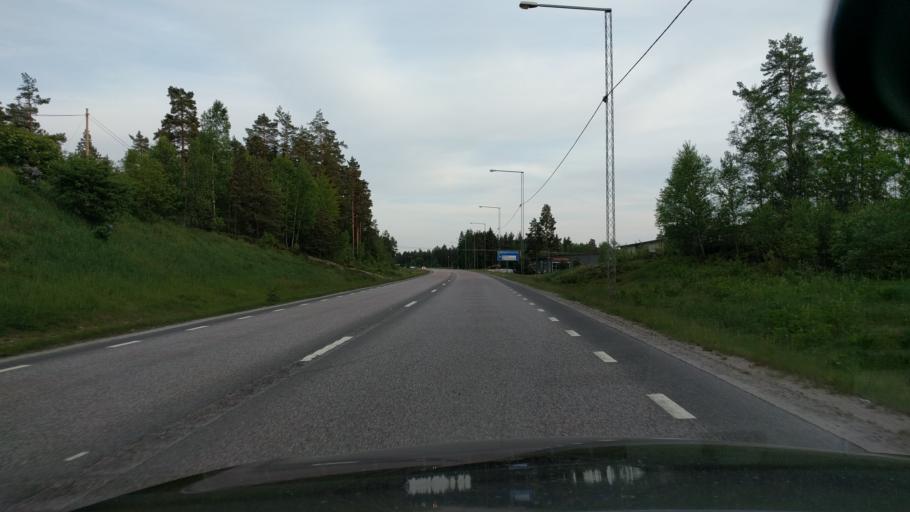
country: SE
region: Stockholm
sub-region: Vallentuna Kommun
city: Vallentuna
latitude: 59.5176
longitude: 18.0939
